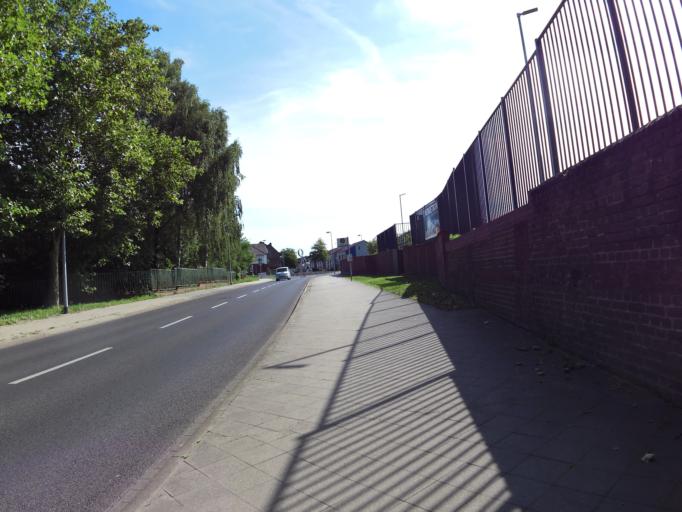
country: DE
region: North Rhine-Westphalia
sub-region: Regierungsbezirk Koln
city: Alsdorf
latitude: 50.8758
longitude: 6.1445
